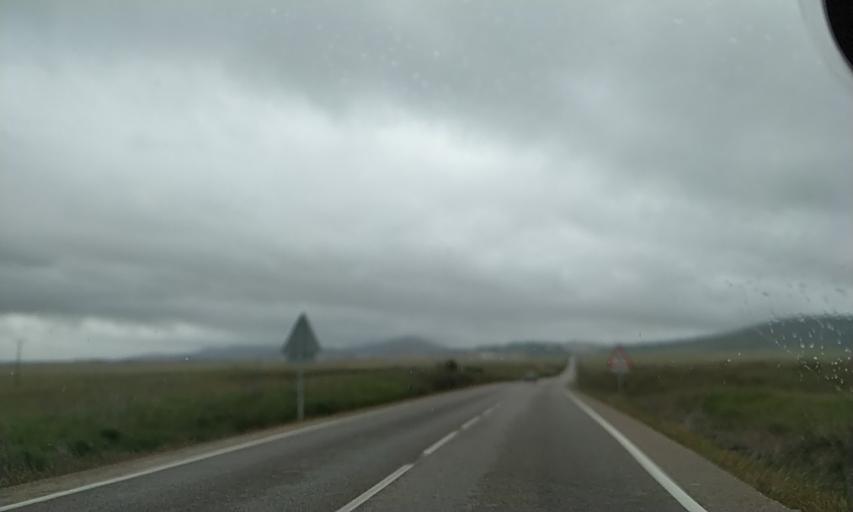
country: ES
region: Extremadura
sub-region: Provincia de Caceres
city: Caceres
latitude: 39.5114
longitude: -6.3941
